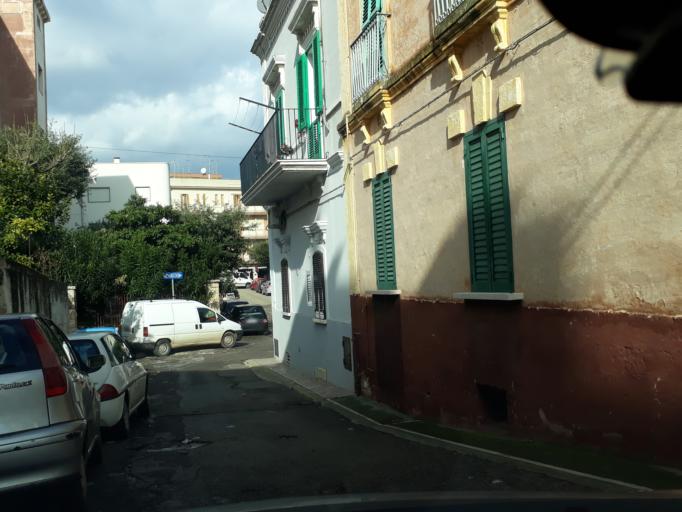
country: IT
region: Apulia
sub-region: Provincia di Brindisi
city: Fasano
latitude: 40.8336
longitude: 17.3559
